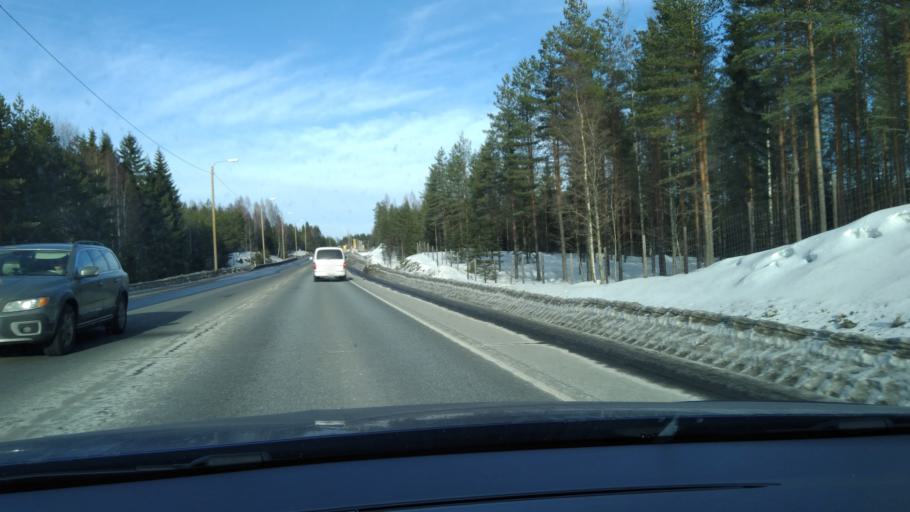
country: FI
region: Pirkanmaa
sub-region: Tampere
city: Orivesi
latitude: 61.6670
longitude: 24.2743
